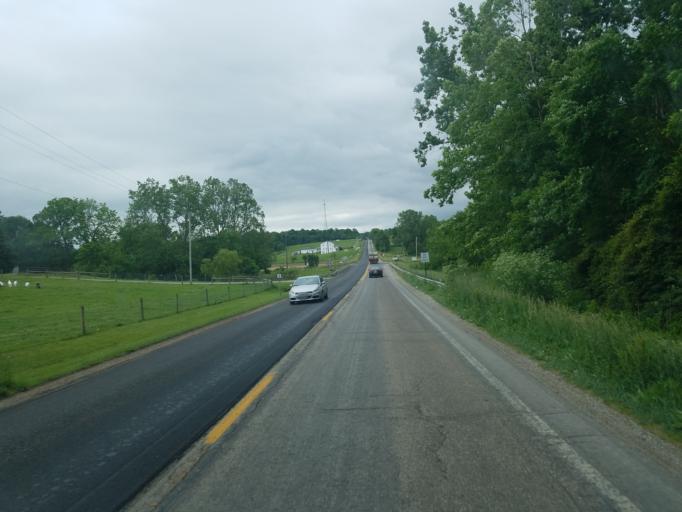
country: US
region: Ohio
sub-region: Knox County
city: Fredericktown
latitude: 40.5516
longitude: -82.6619
